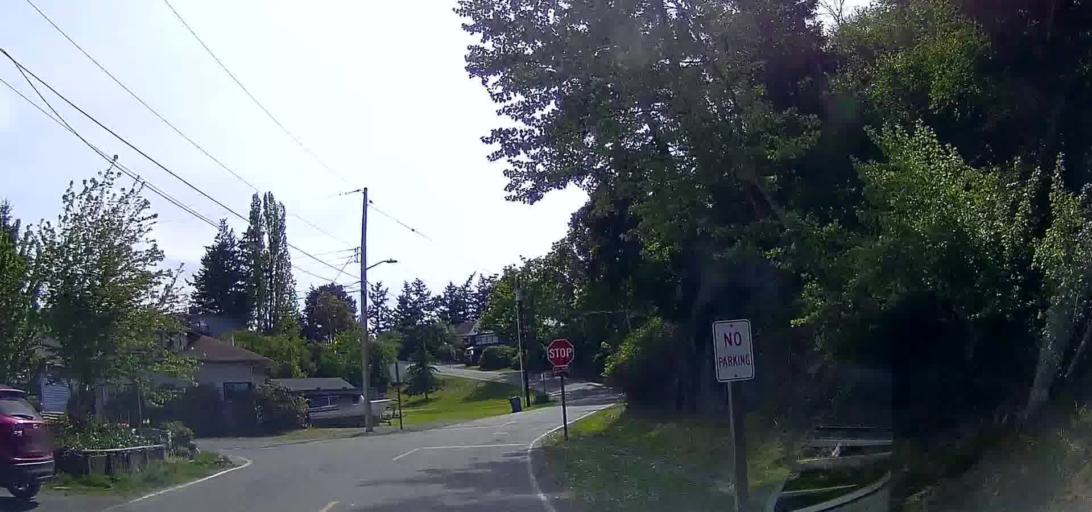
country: US
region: Washington
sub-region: Skagit County
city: Mount Vernon
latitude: 48.3893
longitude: -122.4936
